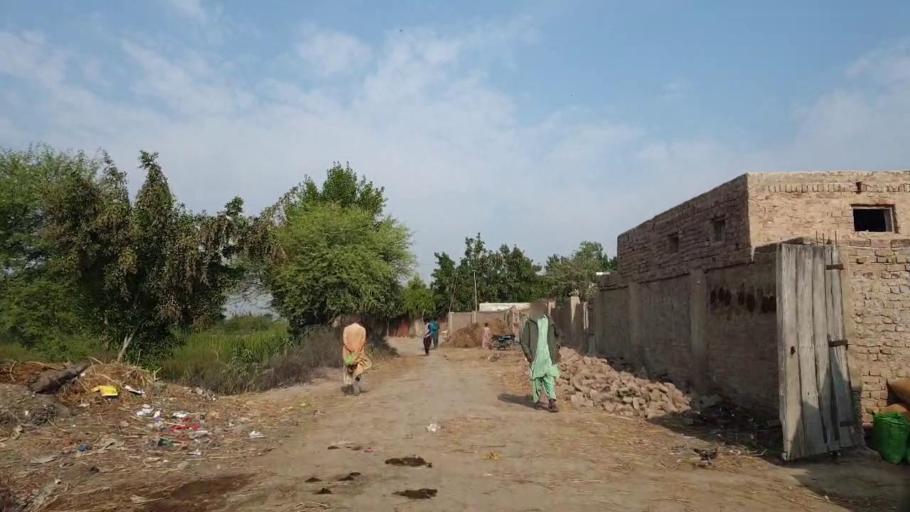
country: PK
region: Sindh
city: Tando Muhammad Khan
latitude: 25.0512
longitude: 68.4356
